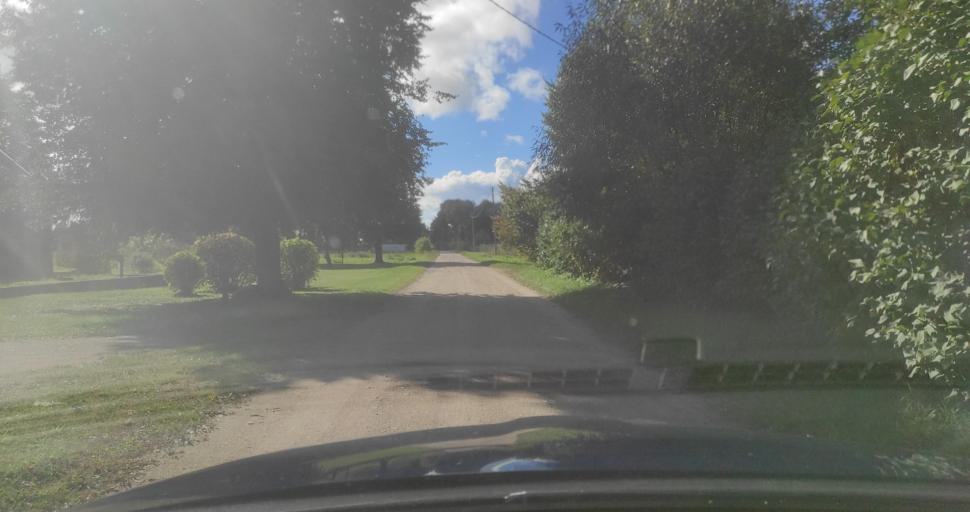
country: LV
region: Ventspils
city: Ventspils
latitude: 57.3677
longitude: 21.6267
